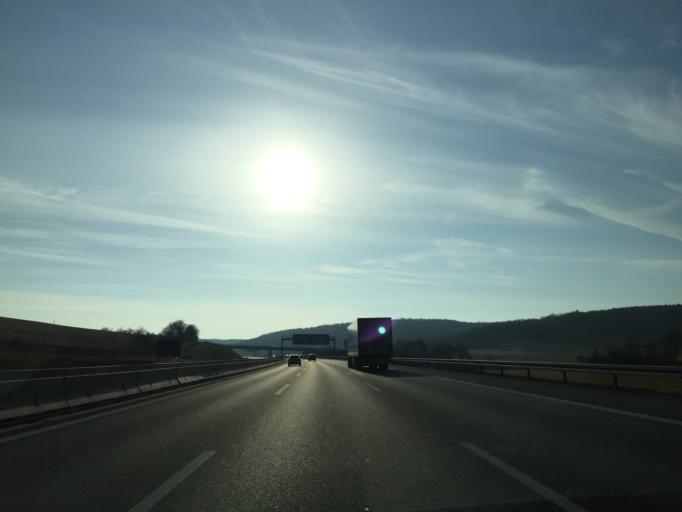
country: DE
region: Bavaria
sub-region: Regierungsbezirk Unterfranken
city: Waldbrunn
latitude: 49.7539
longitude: 9.7888
